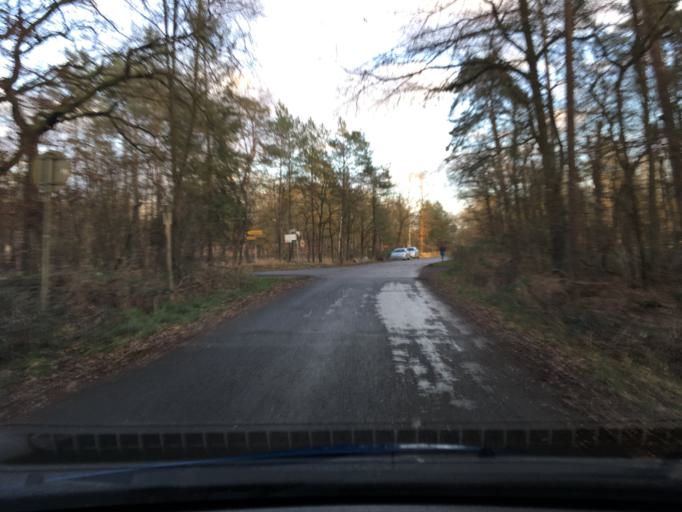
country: DE
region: Lower Saxony
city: Oldendorf
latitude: 53.1417
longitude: 10.1986
